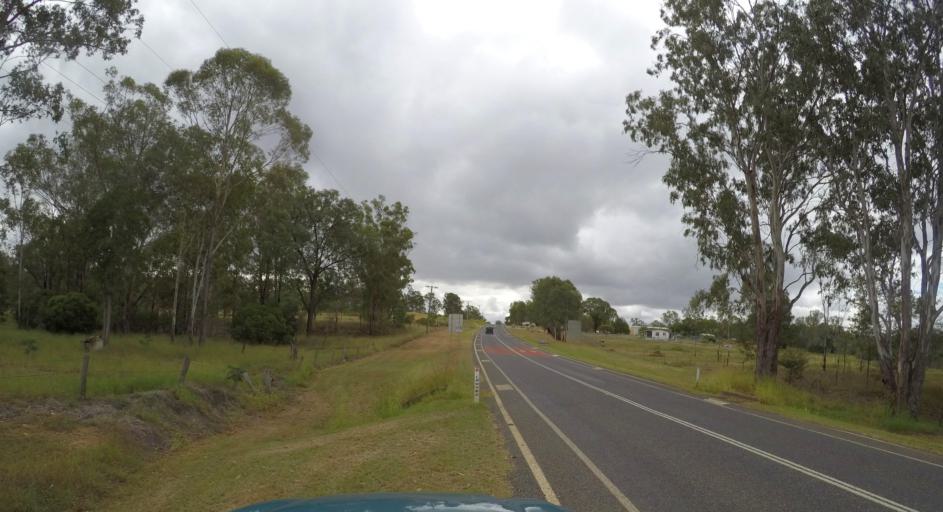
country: AU
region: Queensland
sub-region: North Burnett
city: Gayndah
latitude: -25.3639
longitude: 151.1202
